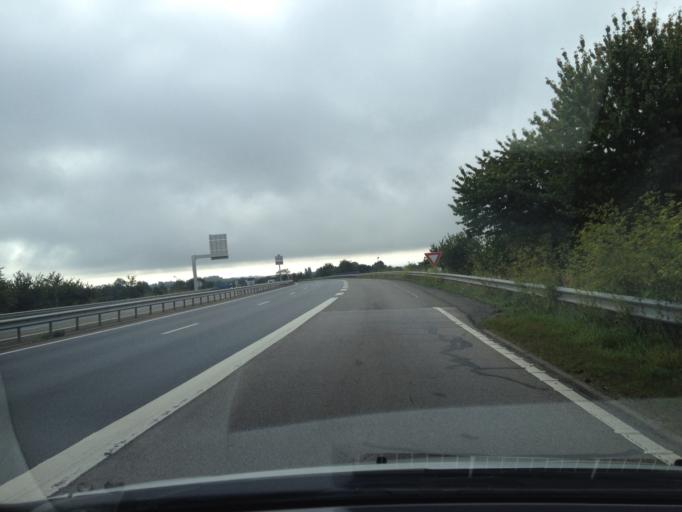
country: FR
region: Lower Normandy
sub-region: Departement de l'Orne
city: Valframbert
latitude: 48.4537
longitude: 0.0983
